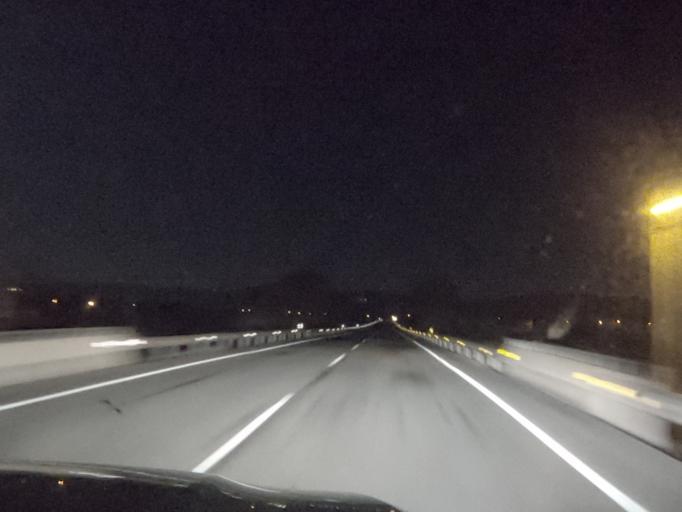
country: ES
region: Galicia
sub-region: Provincia de Ourense
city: Verin
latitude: 41.9524
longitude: -7.4962
